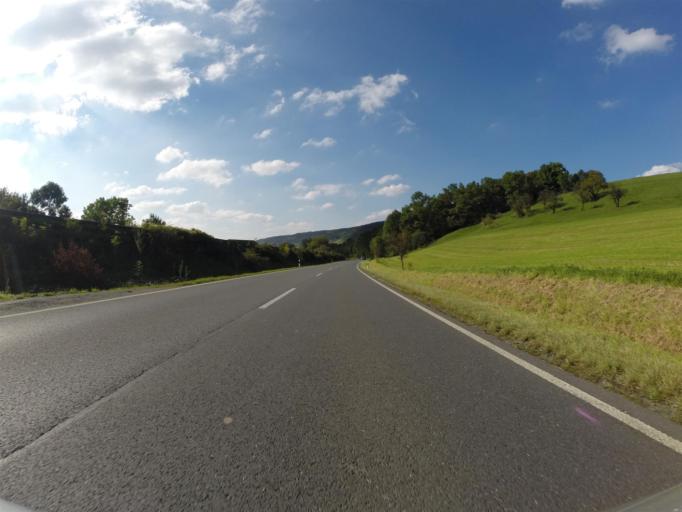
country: DE
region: Thuringia
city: Grosslobichau
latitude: 50.9286
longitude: 11.6862
